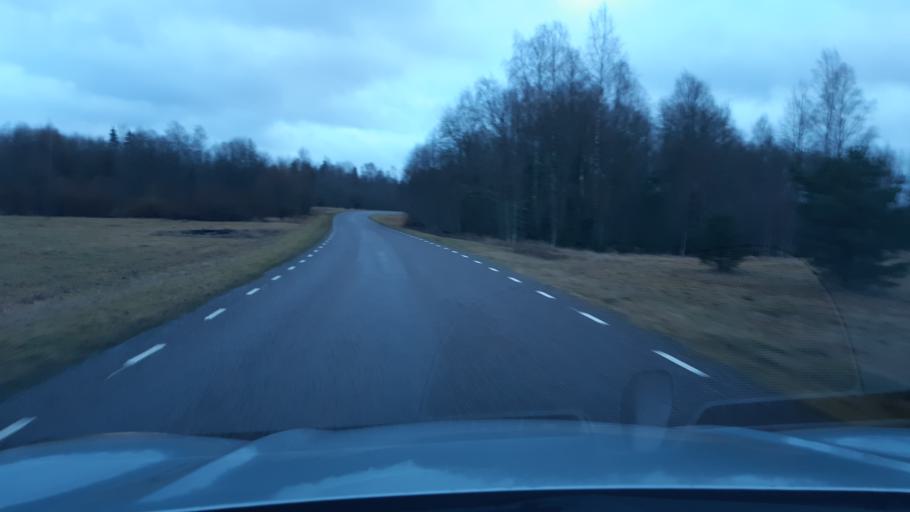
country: EE
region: Raplamaa
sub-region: Rapla vald
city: Rapla
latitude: 58.9861
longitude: 24.7312
